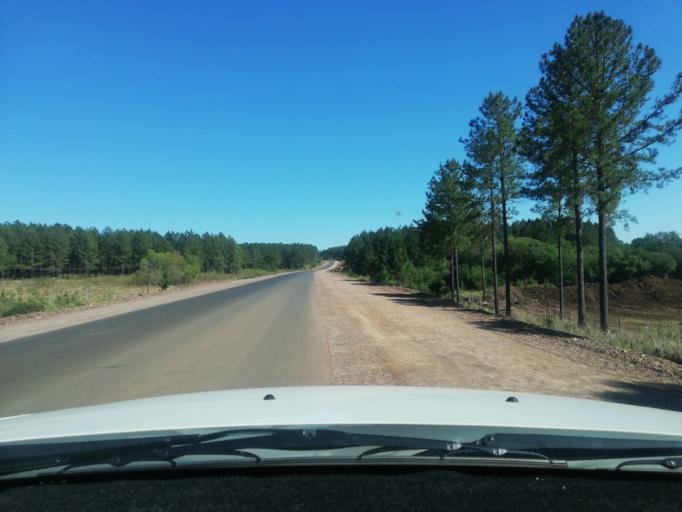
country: AR
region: Misiones
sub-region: Departamento de Candelaria
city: Candelaria
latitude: -27.5272
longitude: -55.7217
